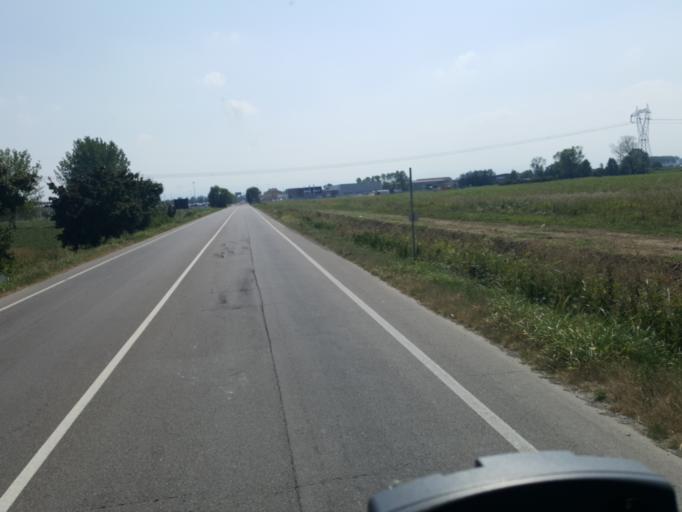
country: IT
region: Emilia-Romagna
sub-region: Provincia di Piacenza
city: Caorso
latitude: 45.0662
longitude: 9.8871
